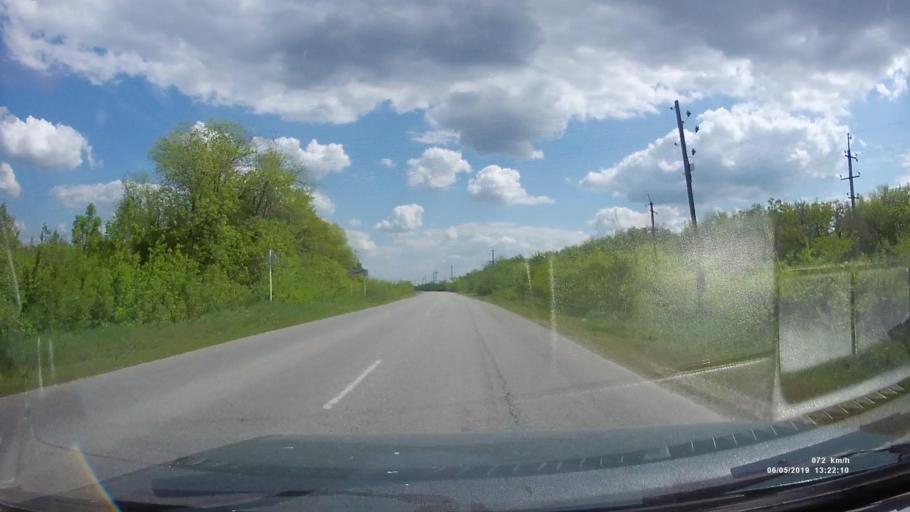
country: RU
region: Rostov
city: Ust'-Donetskiy
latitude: 47.6983
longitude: 40.9167
